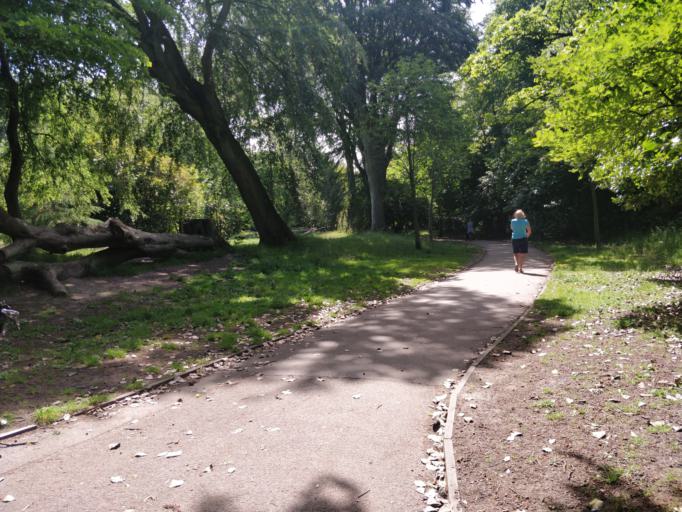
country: GB
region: England
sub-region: Lancashire
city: Banks
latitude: 53.6636
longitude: -2.9590
